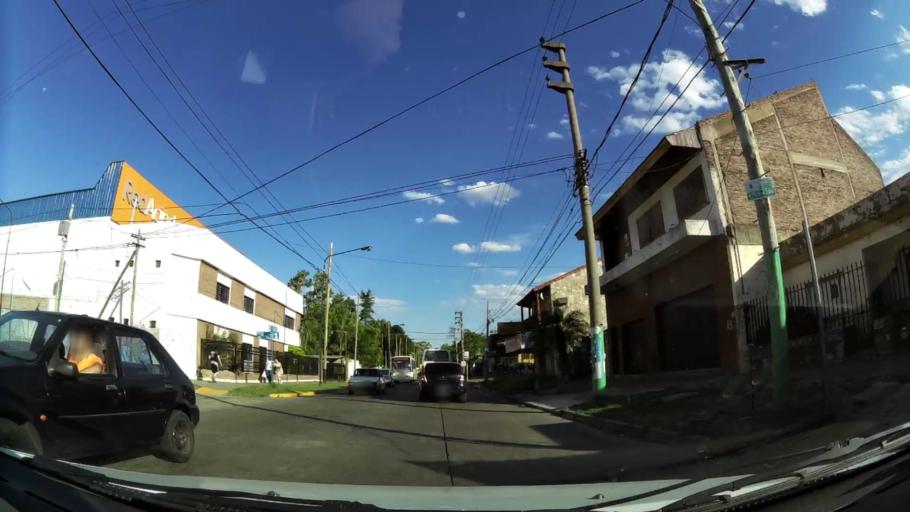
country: AR
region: Buenos Aires
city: Hurlingham
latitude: -34.5794
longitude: -58.6042
